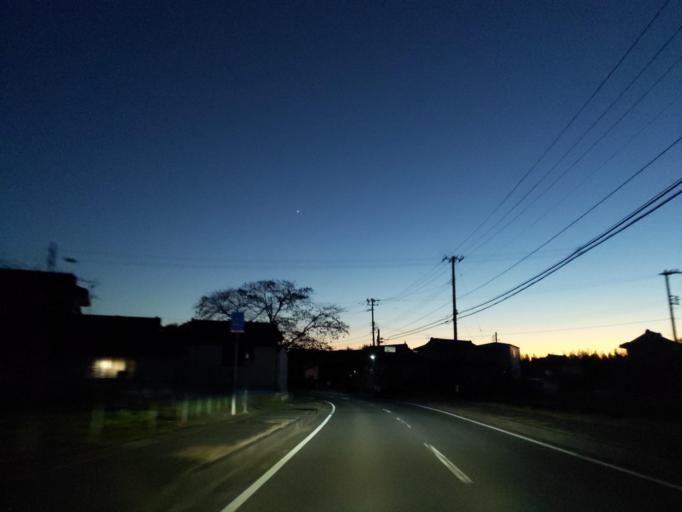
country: JP
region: Fukushima
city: Sukagawa
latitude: 37.3098
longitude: 140.3818
